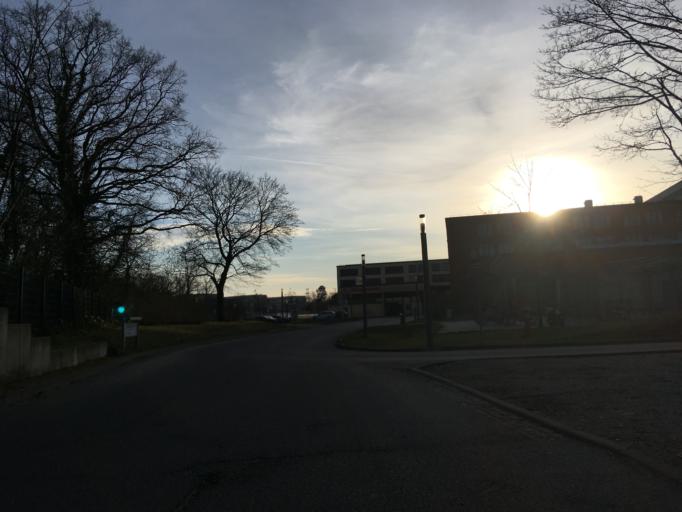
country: DE
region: Berlin
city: Buch
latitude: 52.6315
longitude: 13.5124
